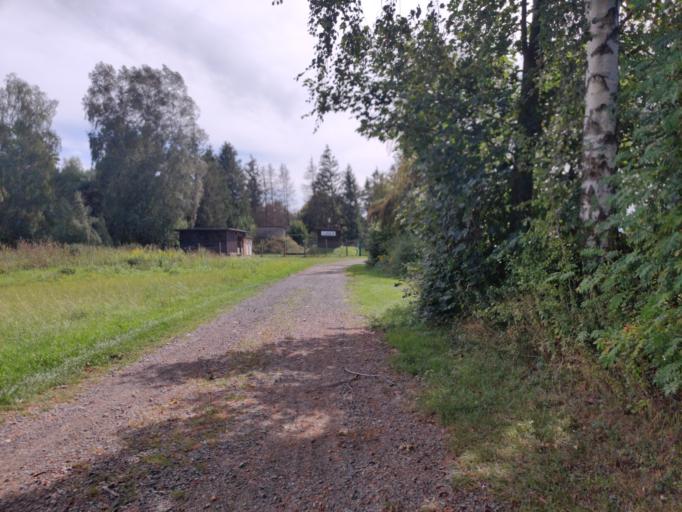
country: DE
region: Lower Saxony
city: Langelsheim
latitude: 51.9769
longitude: 10.3697
